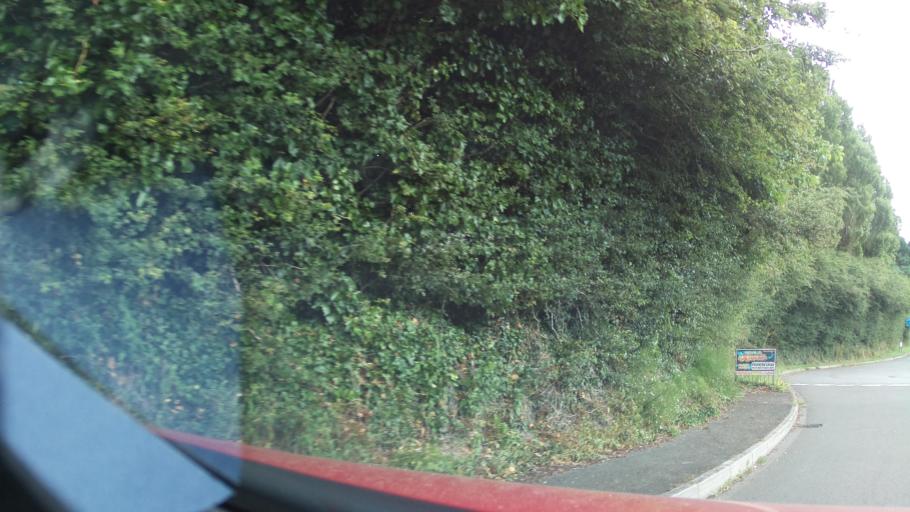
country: GB
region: England
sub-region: Borough of Torbay
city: Torquay
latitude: 50.4889
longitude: -3.5265
